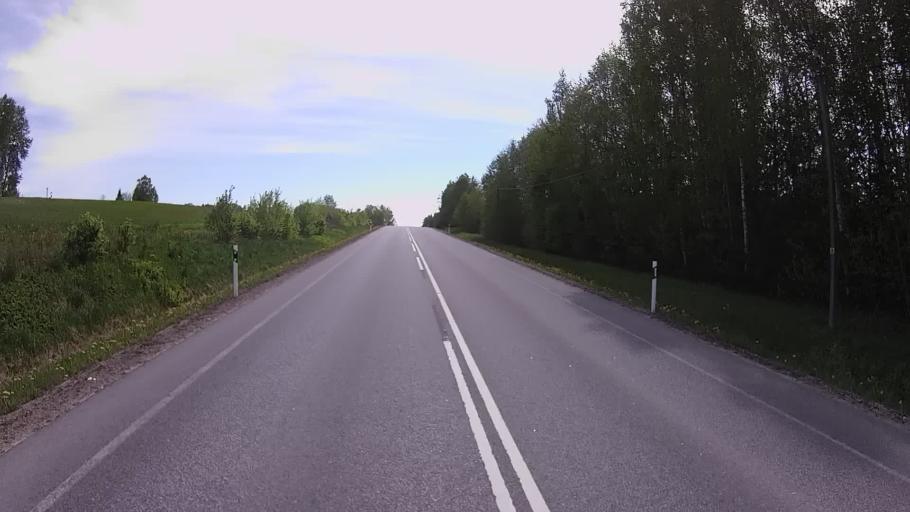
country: EE
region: Valgamaa
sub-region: Valga linn
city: Valga
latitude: 57.7459
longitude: 26.1419
